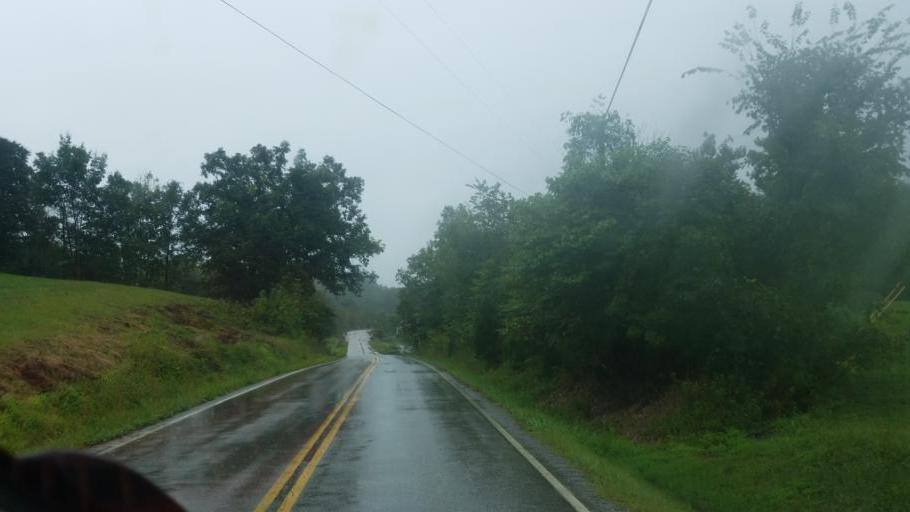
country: US
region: Kentucky
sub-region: Greenup County
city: South Shore
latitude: 38.6718
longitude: -82.9247
